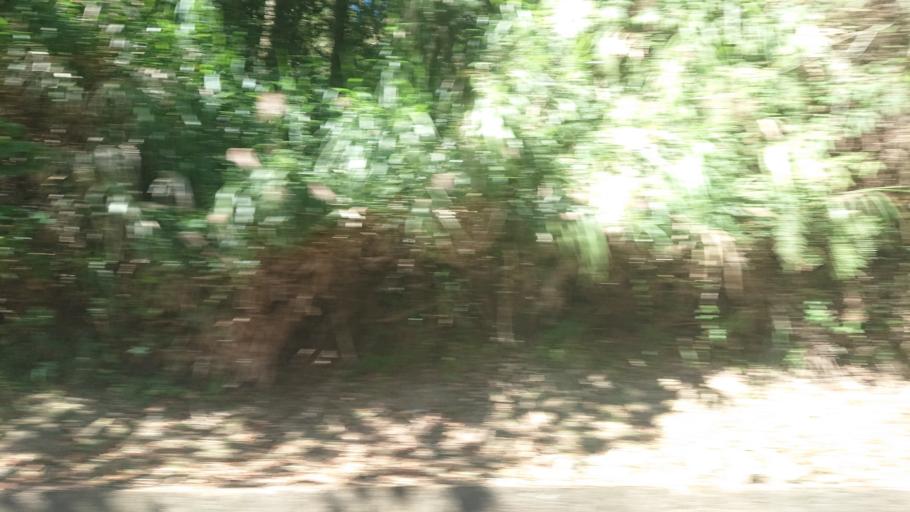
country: TW
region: Taiwan
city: Lugu
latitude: 23.4959
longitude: 120.7788
